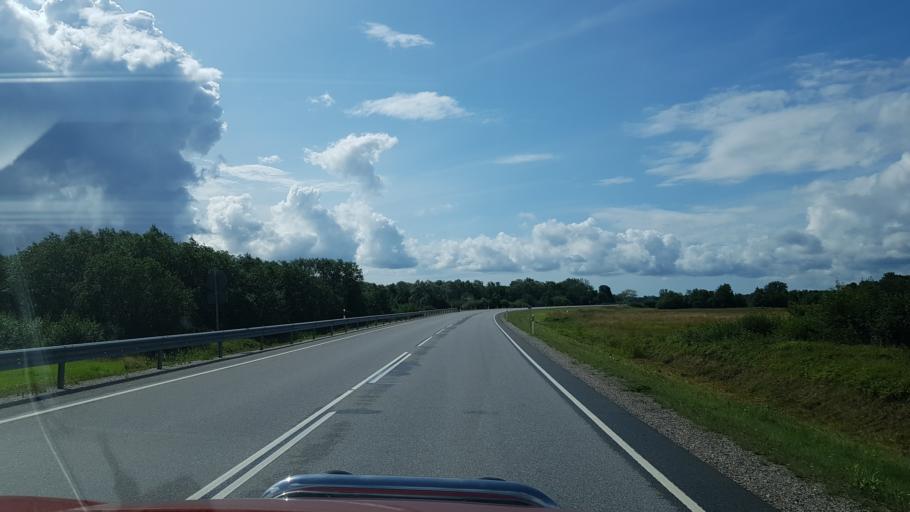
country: EE
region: Laeaene
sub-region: Lihula vald
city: Lihula
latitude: 58.7376
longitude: 23.9958
